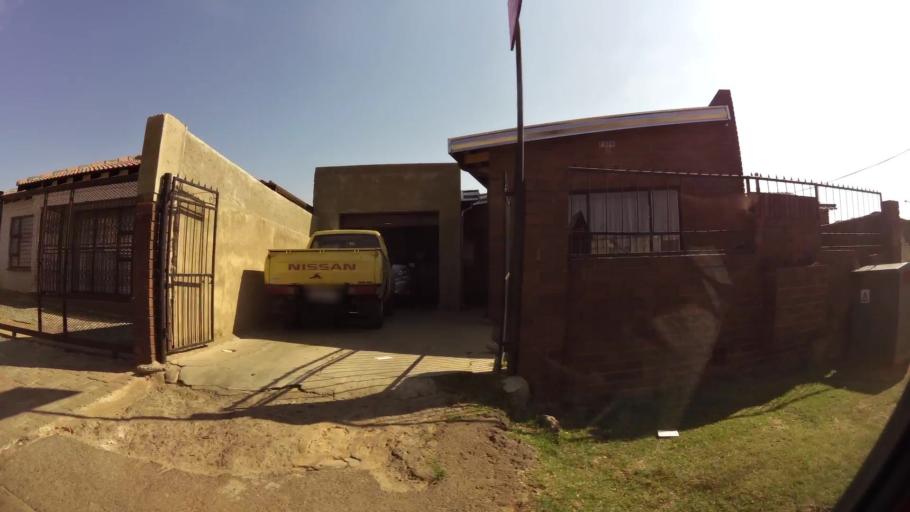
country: ZA
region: Gauteng
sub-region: City of Johannesburg Metropolitan Municipality
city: Johannesburg
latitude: -26.2436
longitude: 27.9567
